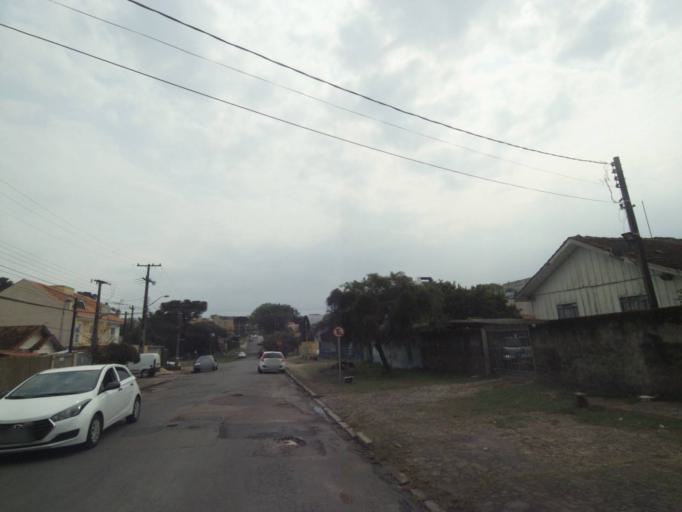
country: BR
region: Parana
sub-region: Curitiba
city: Curitiba
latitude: -25.4800
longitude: -49.2999
